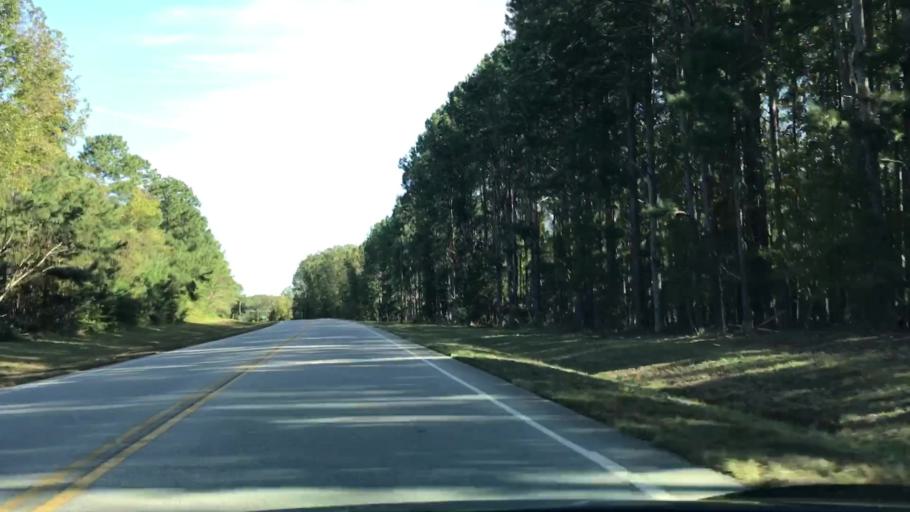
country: US
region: Georgia
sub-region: Warren County
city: Firing Range
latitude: 33.4650
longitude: -82.7115
